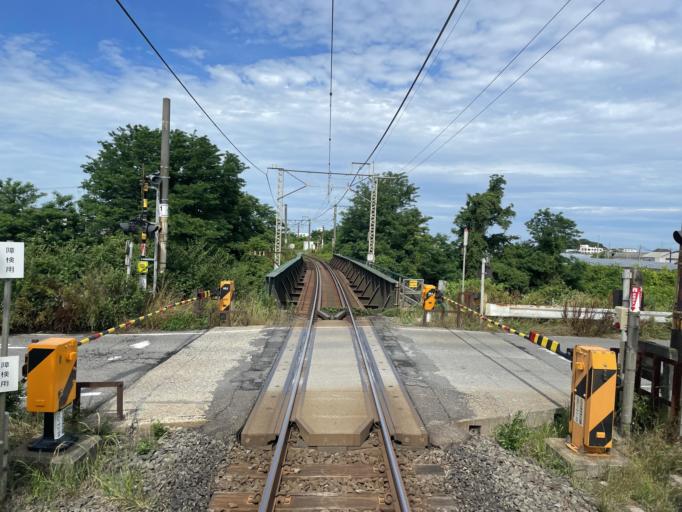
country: JP
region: Niigata
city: Kameda-honcho
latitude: 37.9236
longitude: 139.1639
